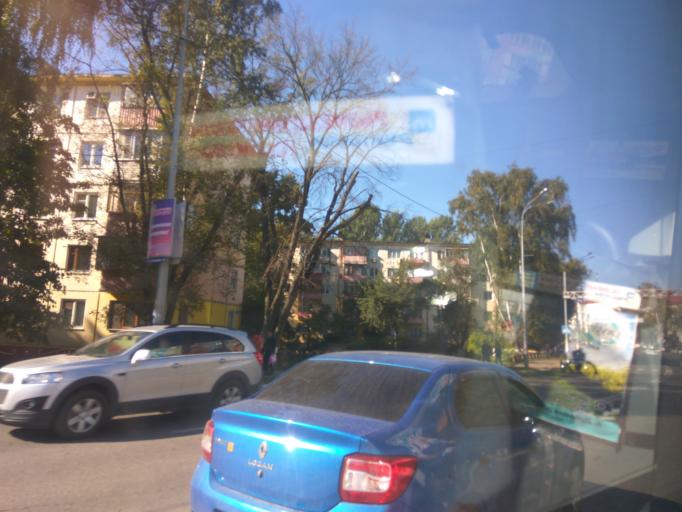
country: RU
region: Moskovskaya
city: Ramenskoye
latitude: 55.5667
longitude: 38.2329
